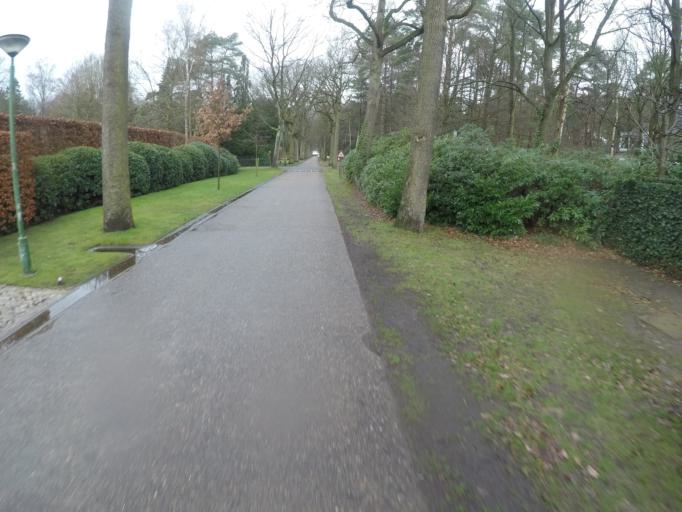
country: BE
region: Flanders
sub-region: Provincie Antwerpen
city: Schilde
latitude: 51.2306
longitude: 4.5652
